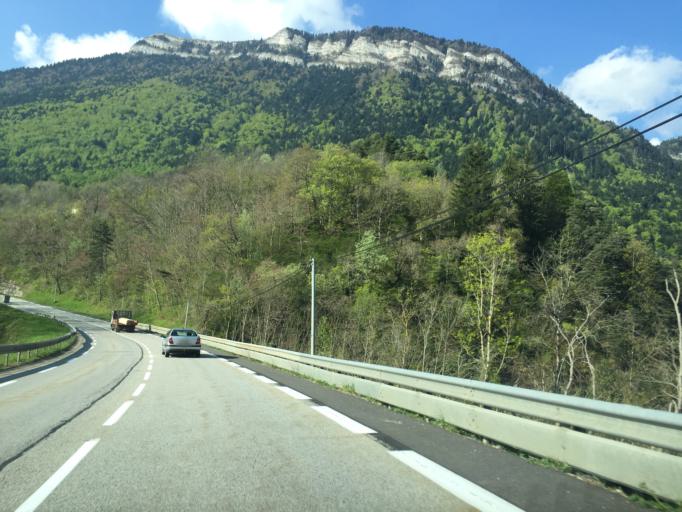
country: FR
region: Rhone-Alpes
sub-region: Departement de l'Isere
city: La Motte-Saint-Martin
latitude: 44.8656
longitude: 5.5988
